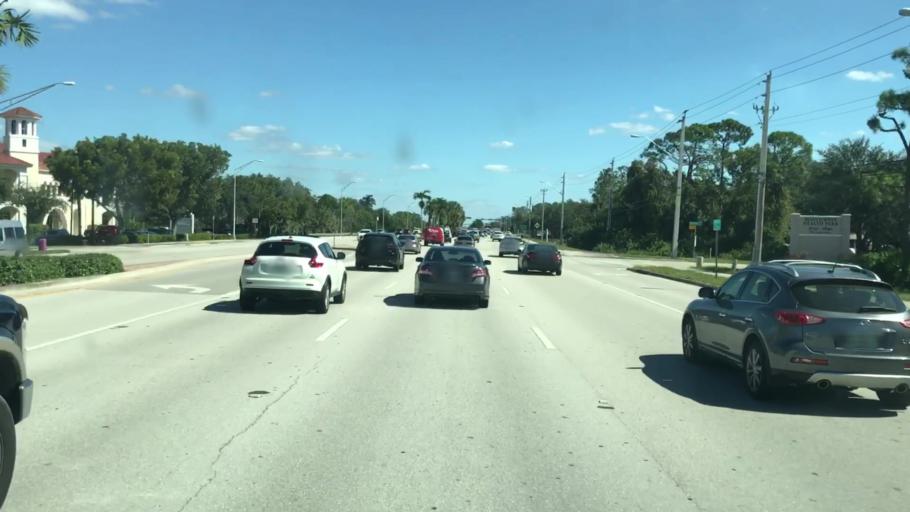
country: US
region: Florida
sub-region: Collier County
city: Naples Park
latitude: 26.2723
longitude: -81.7857
